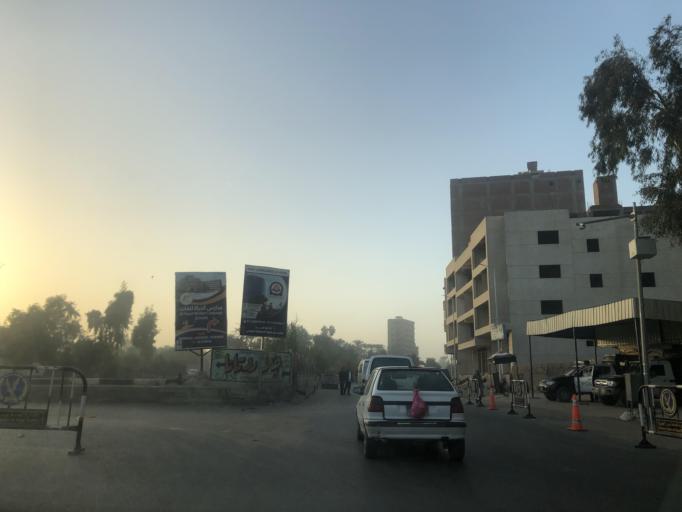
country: EG
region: Al Jizah
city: Al Jizah
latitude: 29.9709
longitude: 31.1774
